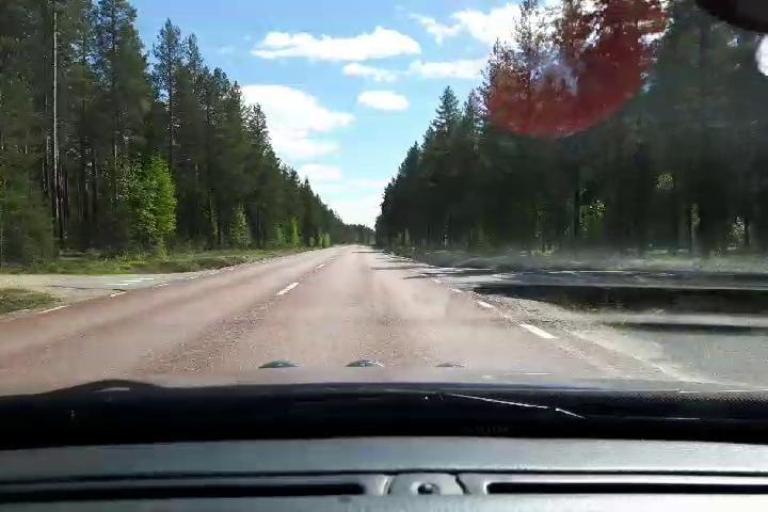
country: SE
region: Gaevleborg
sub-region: Ljusdals Kommun
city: Farila
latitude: 61.8283
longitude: 15.7532
